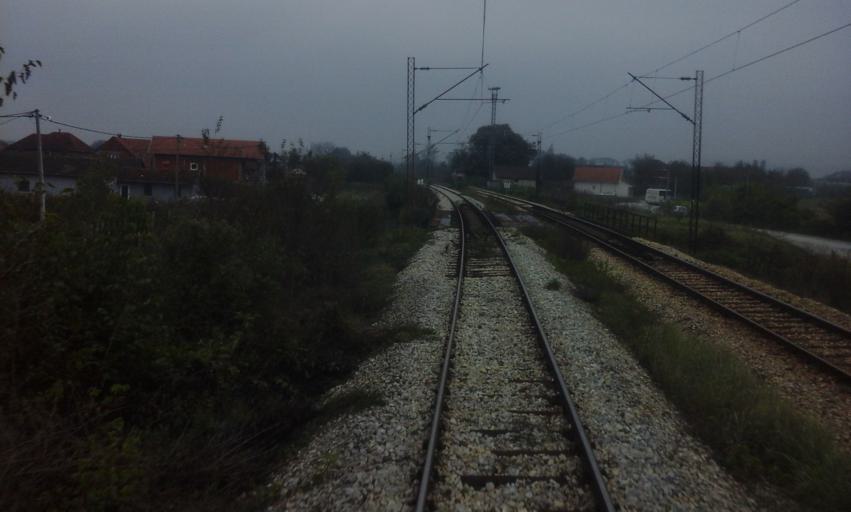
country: RS
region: Central Serbia
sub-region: Pomoravski Okrug
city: Jagodina
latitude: 43.9939
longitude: 21.2409
